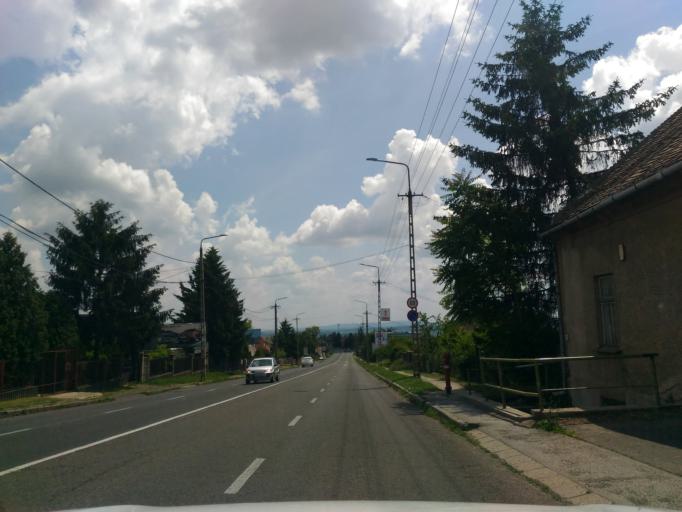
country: HU
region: Baranya
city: Pecs
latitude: 46.1154
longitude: 18.2616
